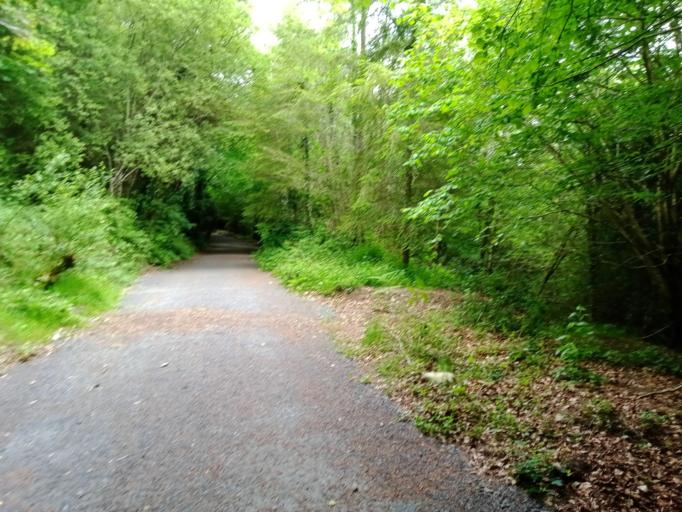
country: IE
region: Leinster
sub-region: Kilkenny
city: Thomastown
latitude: 52.4711
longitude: -7.0456
